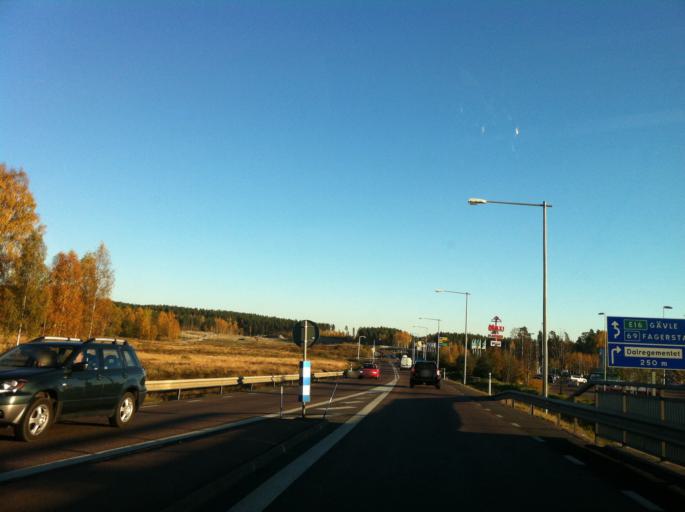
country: SE
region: Dalarna
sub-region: Faluns Kommun
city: Falun
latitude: 60.6089
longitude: 15.6567
